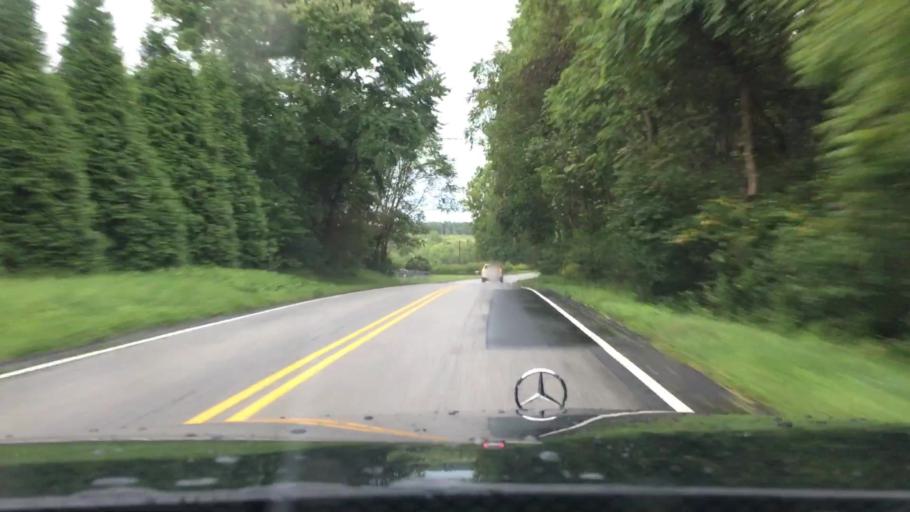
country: US
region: Virginia
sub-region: Amherst County
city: Amherst
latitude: 37.6659
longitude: -79.0115
